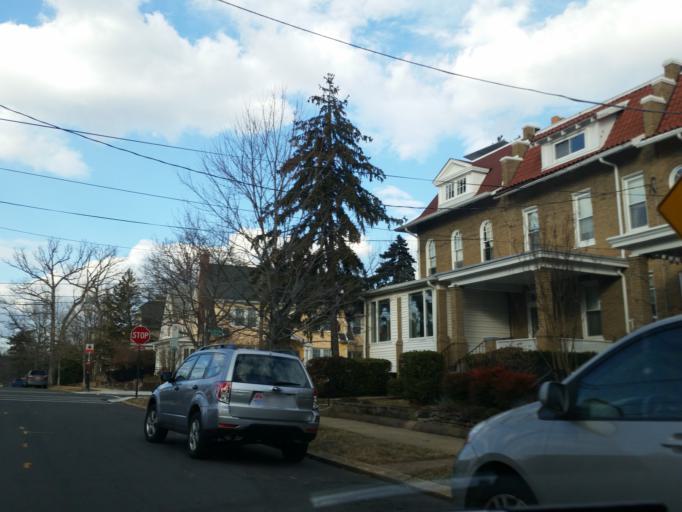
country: US
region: Maryland
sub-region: Montgomery County
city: Takoma Park
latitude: 38.9447
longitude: -77.0388
